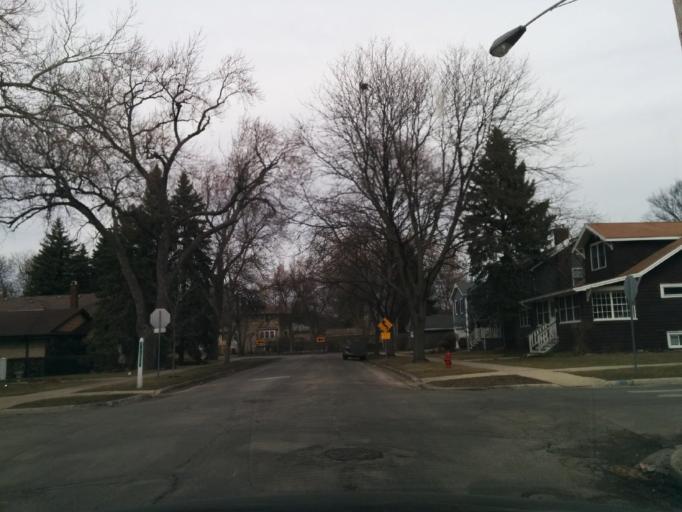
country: US
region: Illinois
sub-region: Cook County
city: La Grange
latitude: 41.8212
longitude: -87.8794
